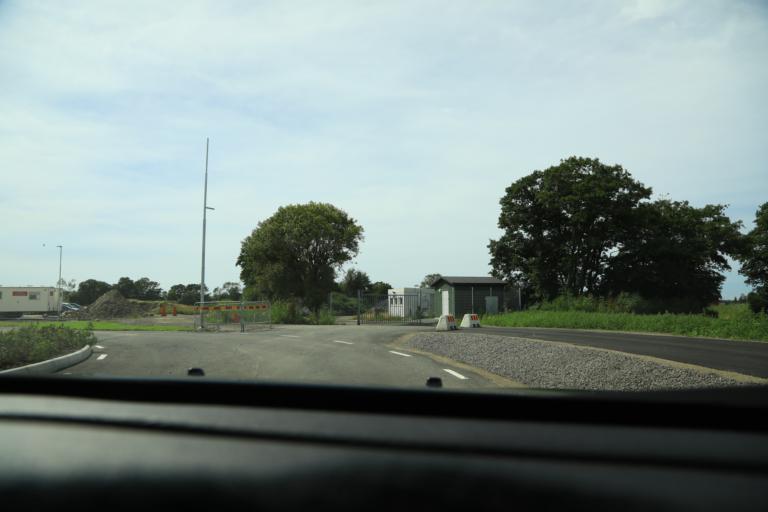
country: SE
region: Halland
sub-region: Varbergs Kommun
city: Varberg
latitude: 57.1387
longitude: 12.2750
